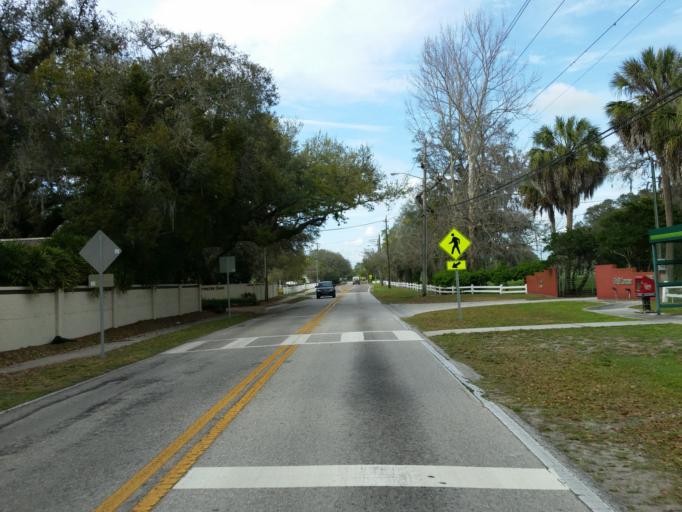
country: US
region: Florida
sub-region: Hillsborough County
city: University
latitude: 28.0721
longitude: -82.4099
